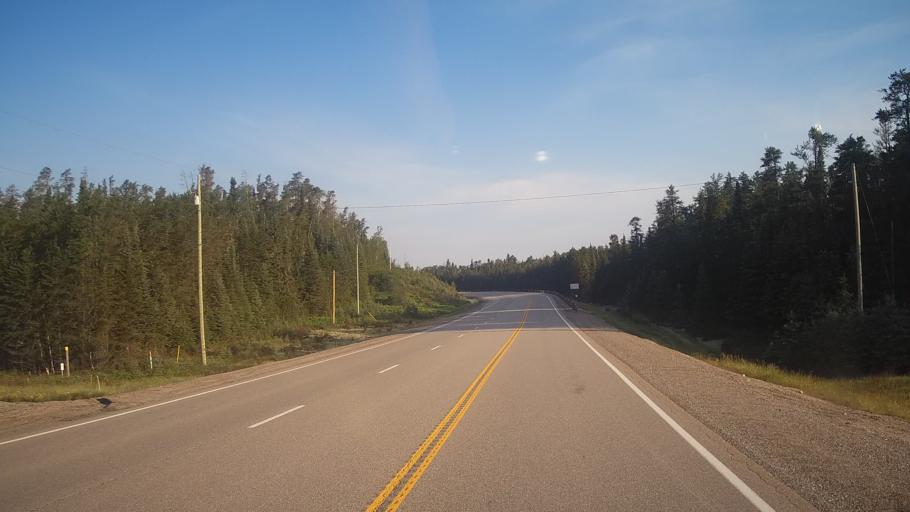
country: CA
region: Ontario
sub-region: Rainy River District
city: Atikokan
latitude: 49.3414
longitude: -91.4768
